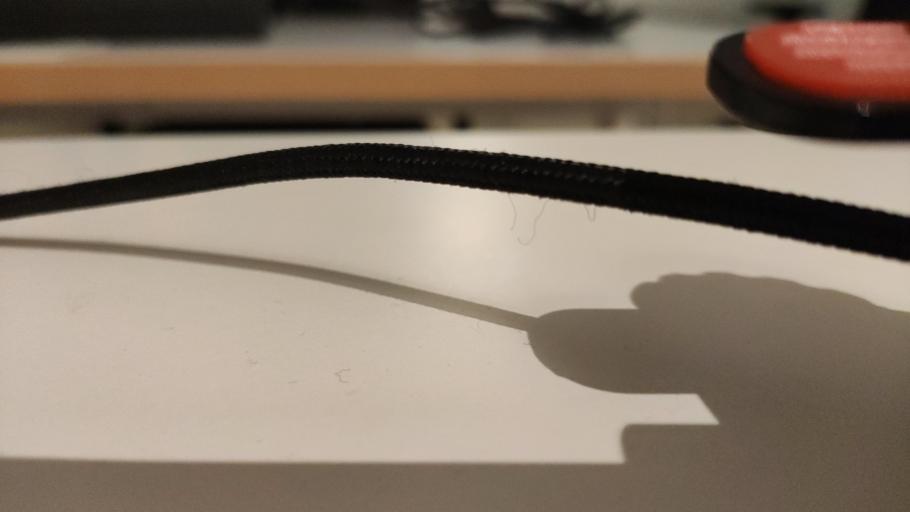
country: RU
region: Moskovskaya
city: Novosin'kovo
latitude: 56.3718
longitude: 37.3448
